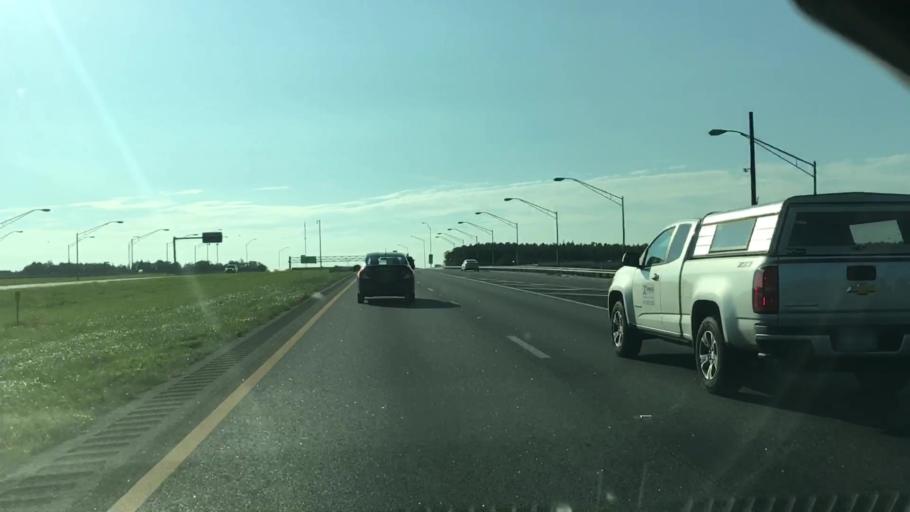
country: US
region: Florida
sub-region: Orange County
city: Hunters Creek
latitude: 28.3734
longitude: -81.4067
